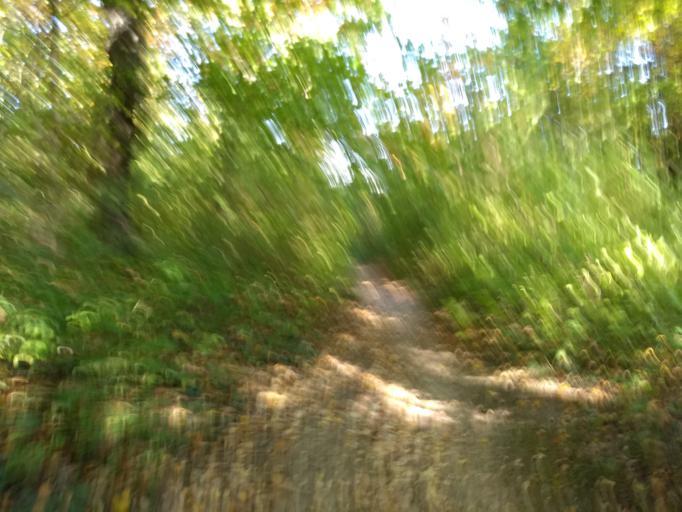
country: AT
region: Lower Austria
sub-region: Politischer Bezirk Modling
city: Giesshubl
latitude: 48.1068
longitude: 16.2405
